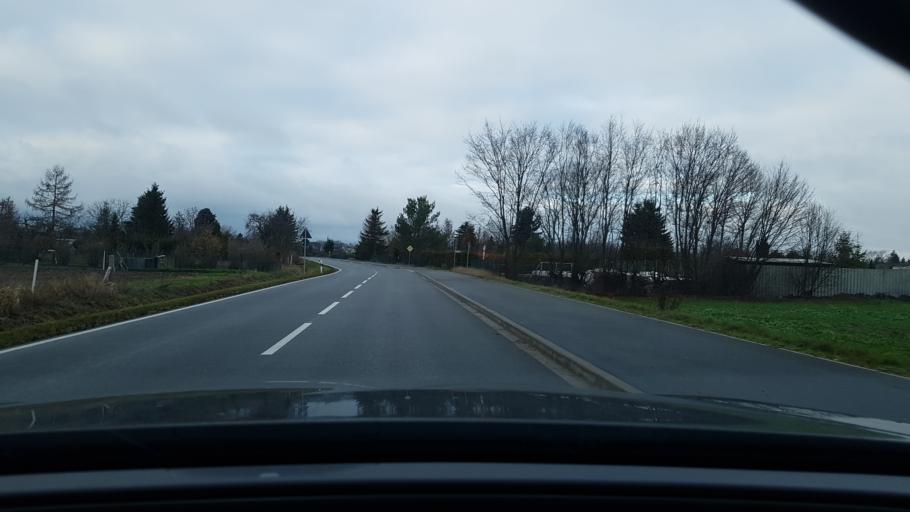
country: DE
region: Saxony-Anhalt
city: Oebisfelde
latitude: 52.4246
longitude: 11.0002
